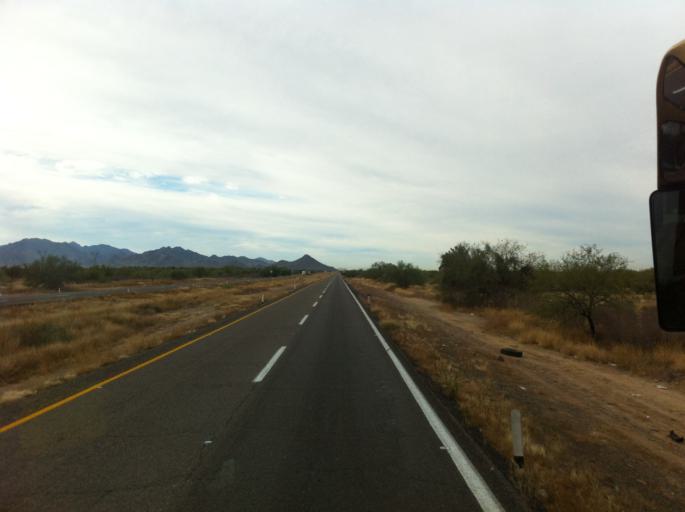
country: MX
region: Sonora
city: Hermosillo
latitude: 28.7114
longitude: -110.9842
